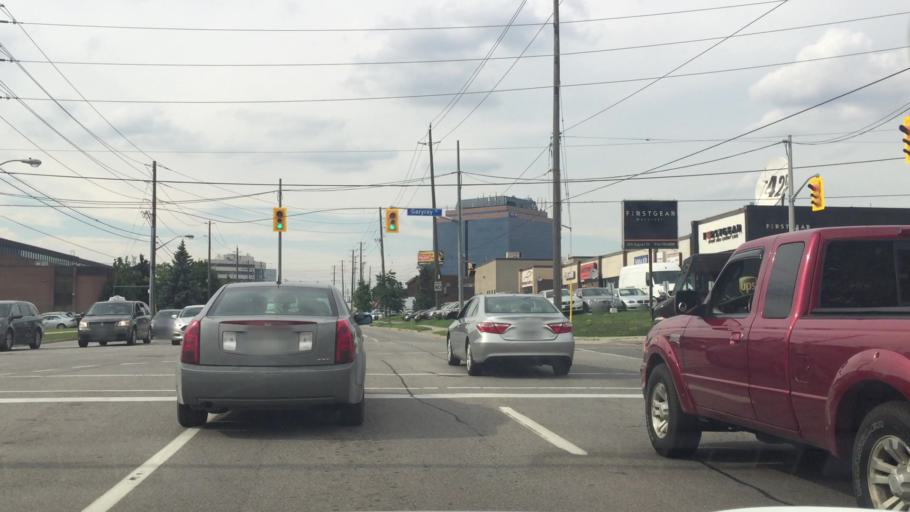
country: CA
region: Ontario
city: Concord
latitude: 43.7683
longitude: -79.5422
